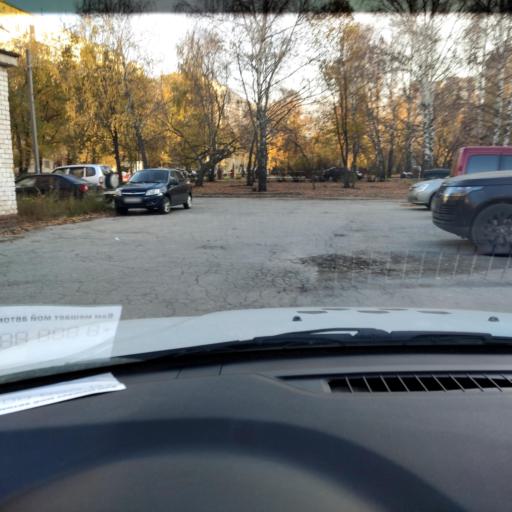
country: RU
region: Samara
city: Tol'yatti
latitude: 53.5056
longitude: 49.4221
